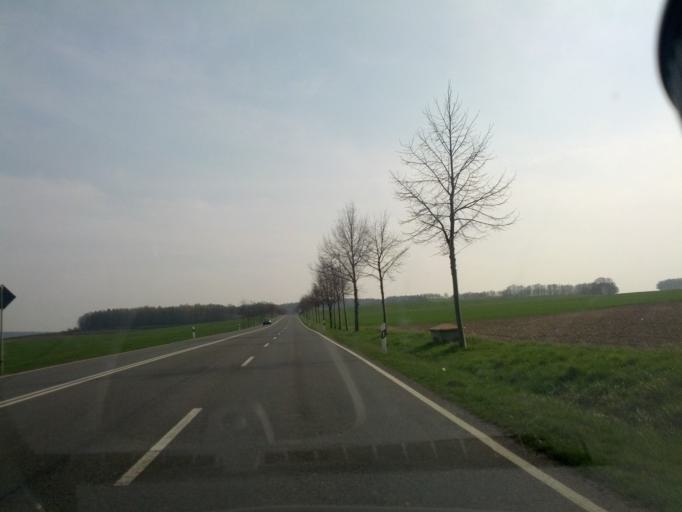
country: DE
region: Saxony
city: Kirchberg
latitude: 50.6443
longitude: 12.5659
